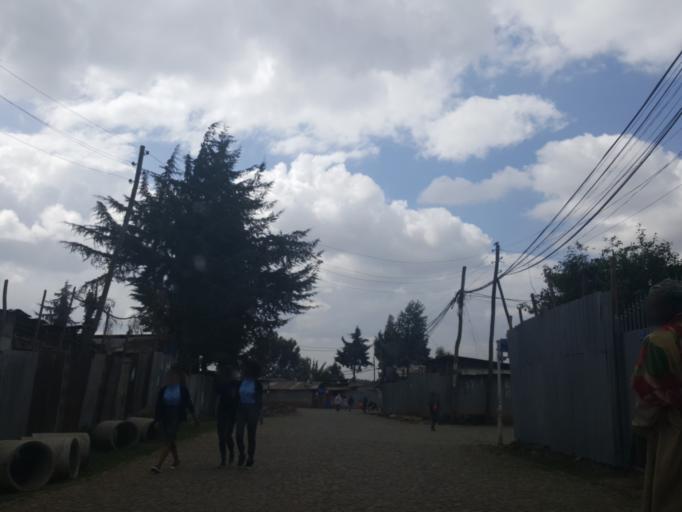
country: ET
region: Adis Abeba
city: Addis Ababa
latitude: 9.0635
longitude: 38.7189
